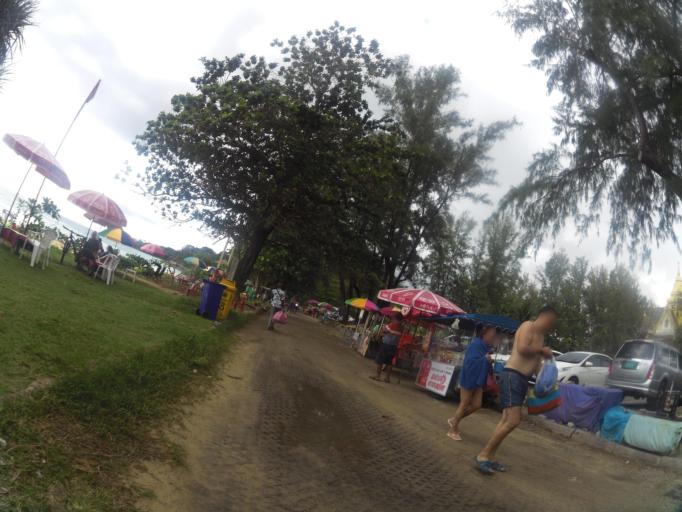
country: TH
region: Phuket
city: Thalang
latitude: 7.9755
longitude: 98.2788
